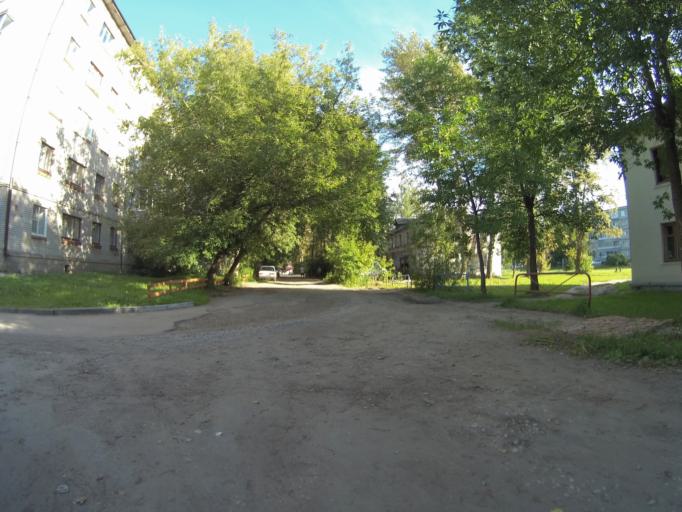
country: RU
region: Vladimir
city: Raduzhnyy
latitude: 56.1012
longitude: 40.2806
